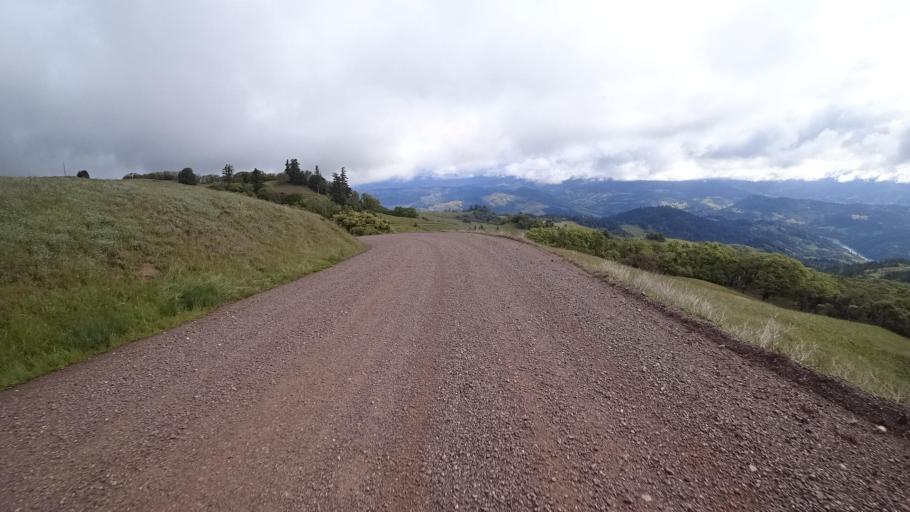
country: US
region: California
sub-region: Humboldt County
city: Redway
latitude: 40.1959
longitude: -123.7018
